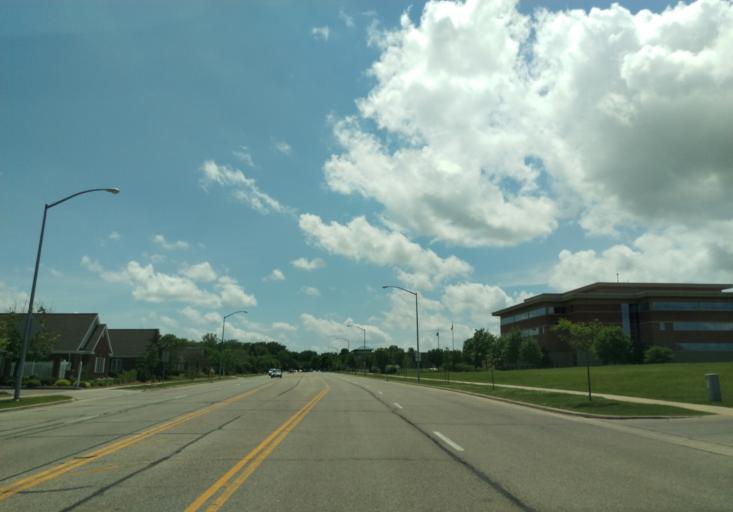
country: US
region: Wisconsin
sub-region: Dane County
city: Middleton
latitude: 43.0783
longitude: -89.5188
